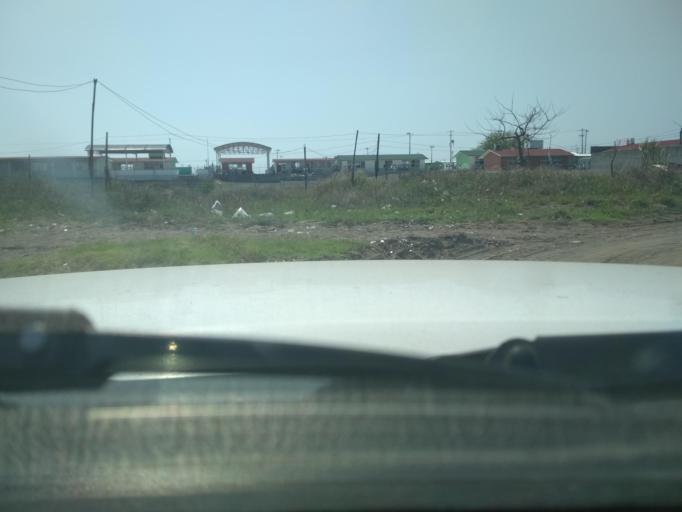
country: MX
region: Veracruz
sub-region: Veracruz
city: Lomas de Rio Medio Cuatro
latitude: 19.1947
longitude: -96.1986
